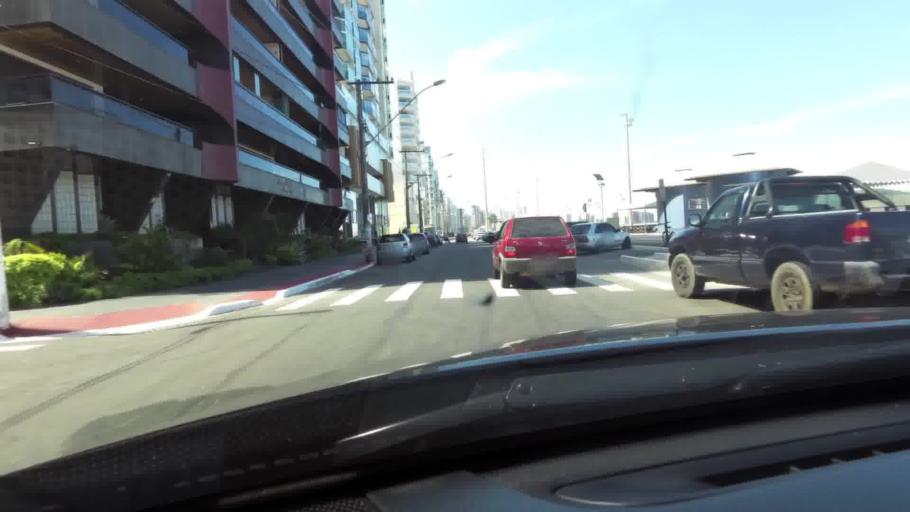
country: BR
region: Espirito Santo
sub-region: Guarapari
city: Guarapari
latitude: -20.6588
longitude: -40.4941
